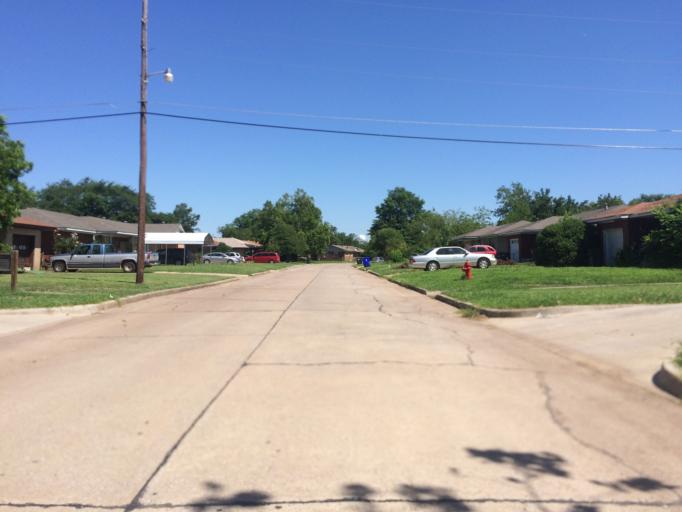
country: US
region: Oklahoma
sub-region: Cleveland County
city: Norman
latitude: 35.2305
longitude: -97.4566
